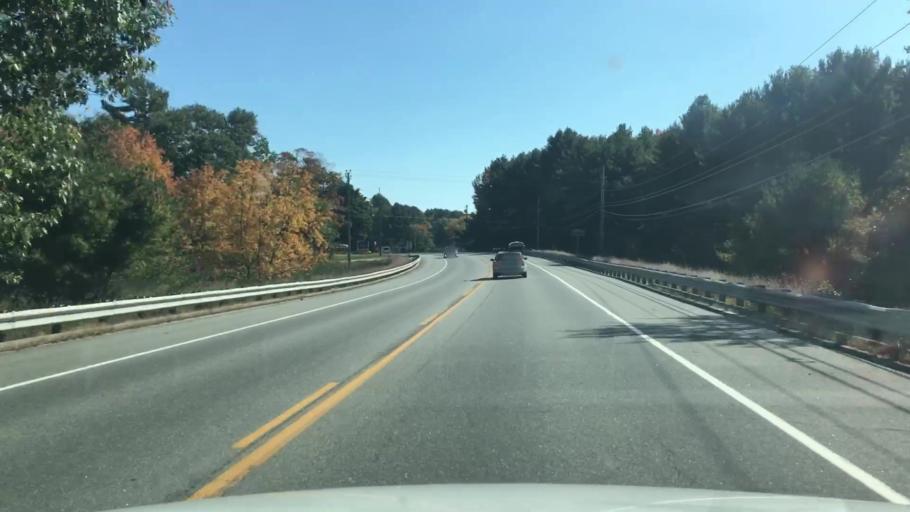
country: US
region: Maine
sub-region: Androscoggin County
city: Lisbon Falls
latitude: 43.9641
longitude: -70.0167
